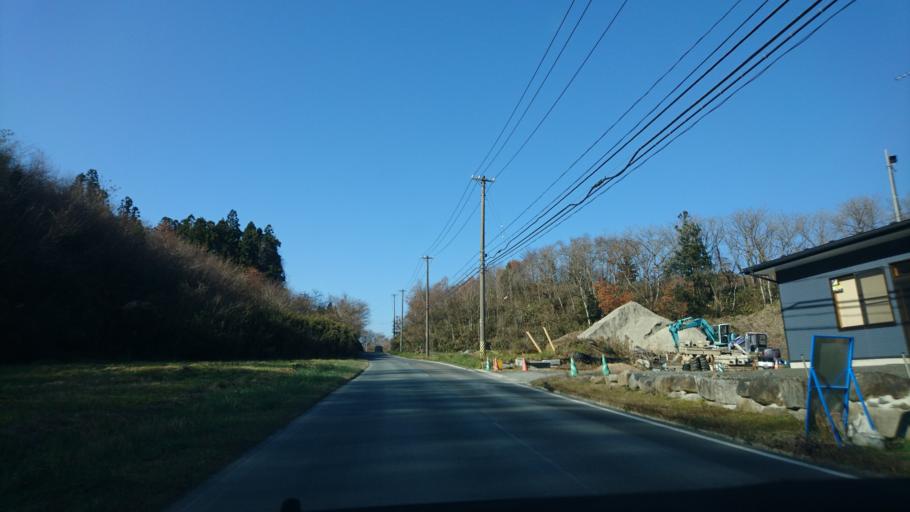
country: JP
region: Iwate
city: Ichinoseki
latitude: 38.9040
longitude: 141.3644
